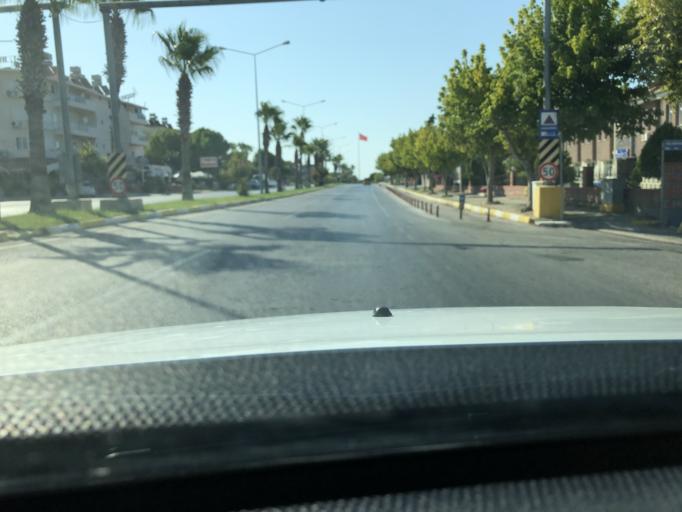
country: TR
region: Antalya
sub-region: Manavgat
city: Side
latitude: 36.7810
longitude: 31.3934
